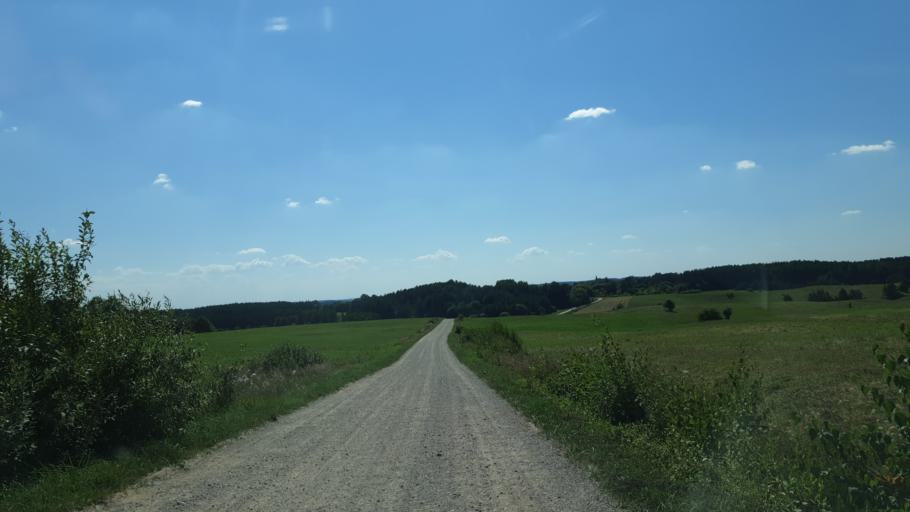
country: LT
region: Vilnius County
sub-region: Vilniaus Rajonas
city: Vievis
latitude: 54.8965
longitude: 24.8660
